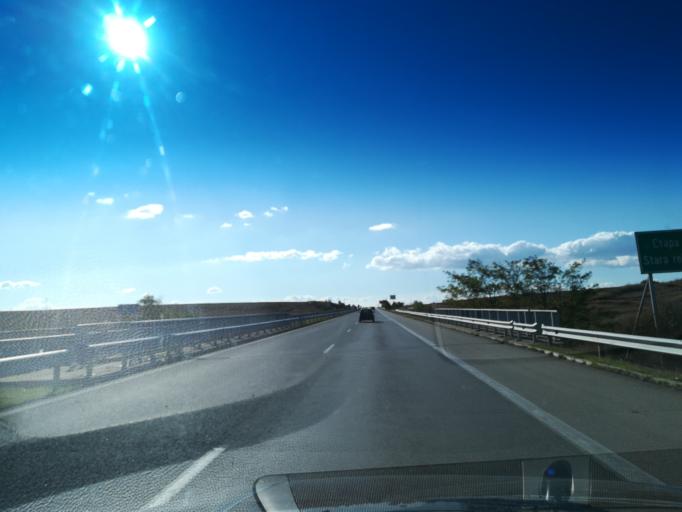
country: BG
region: Stara Zagora
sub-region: Obshtina Chirpan
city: Chirpan
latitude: 42.2394
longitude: 25.3737
